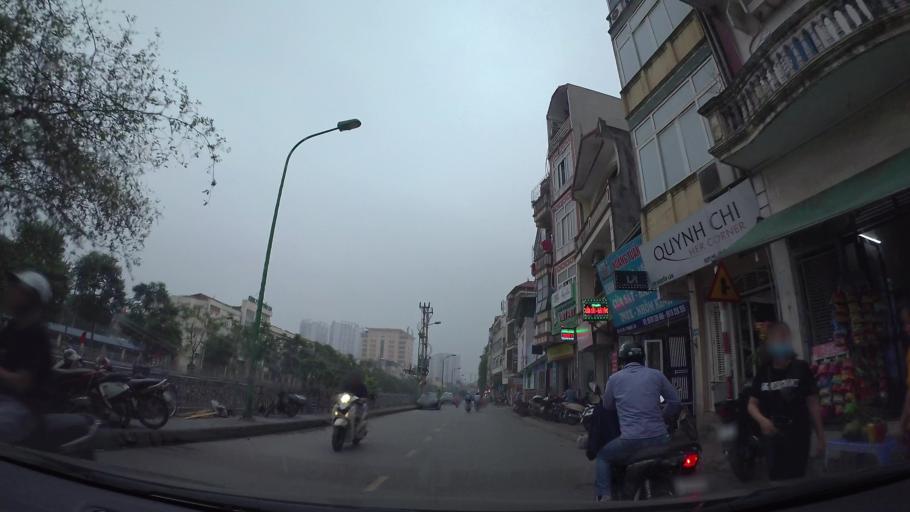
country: VN
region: Ha Noi
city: Hai BaTrung
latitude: 20.9914
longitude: 105.8368
